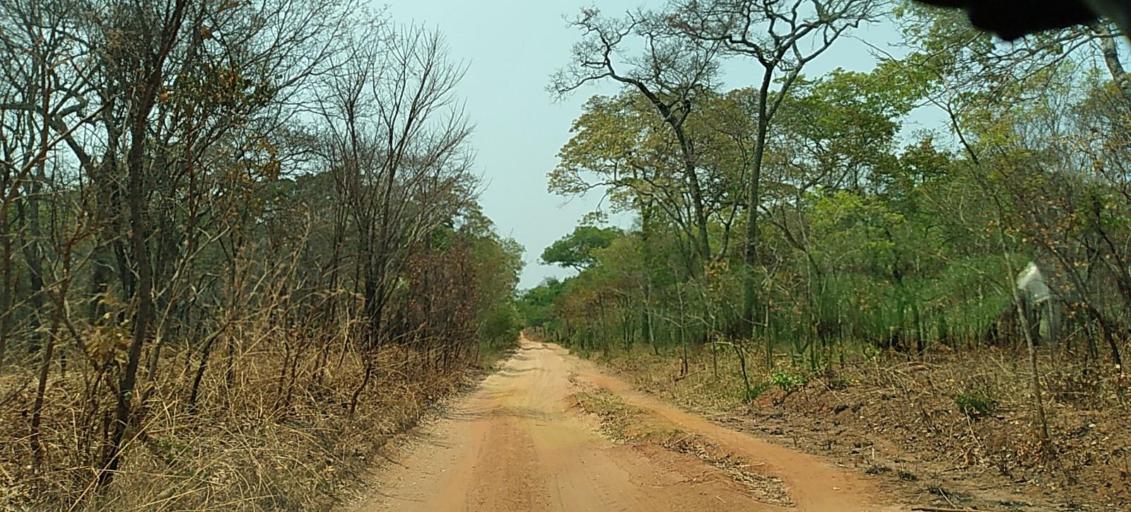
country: ZM
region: North-Western
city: Kabompo
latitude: -13.6908
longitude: 24.3072
